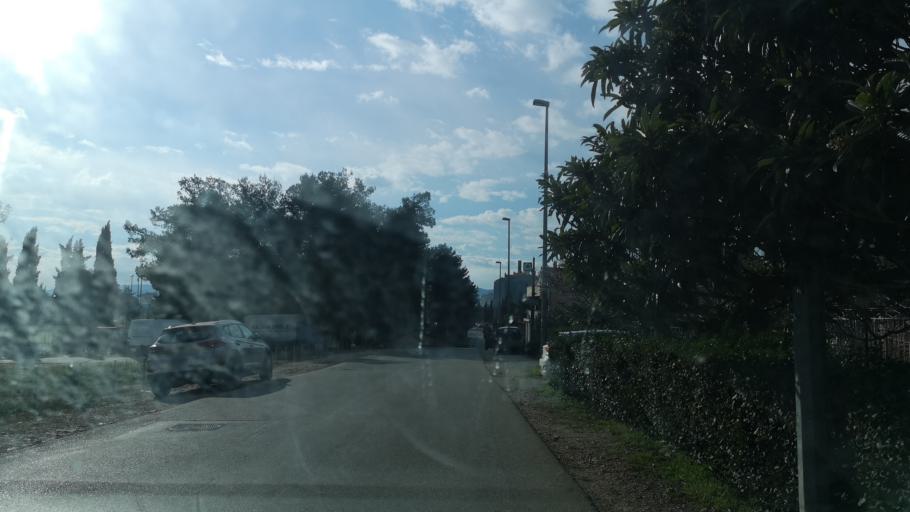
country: HR
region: Zadarska
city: Zadar
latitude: 44.1222
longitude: 15.2440
